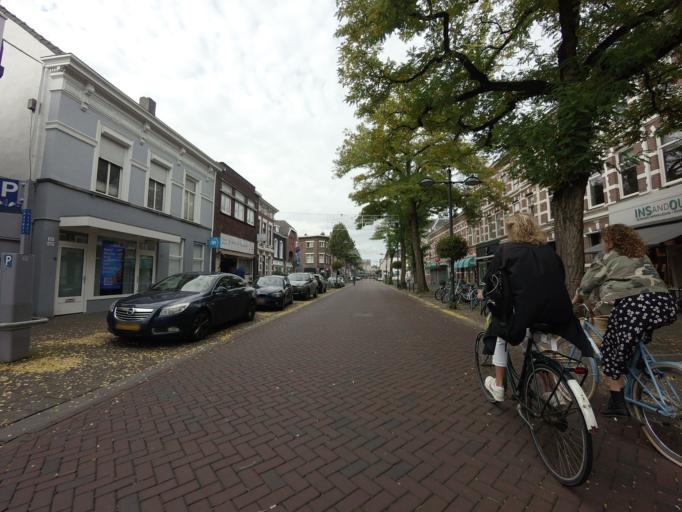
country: NL
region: North Brabant
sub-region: Gemeente Breda
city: Breda
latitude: 51.5775
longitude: 4.7804
